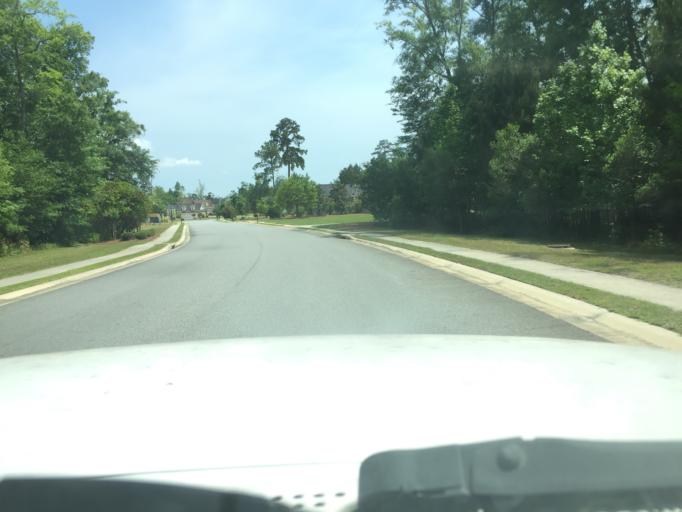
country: US
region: Georgia
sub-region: Chatham County
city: Pooler
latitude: 32.0597
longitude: -81.2420
